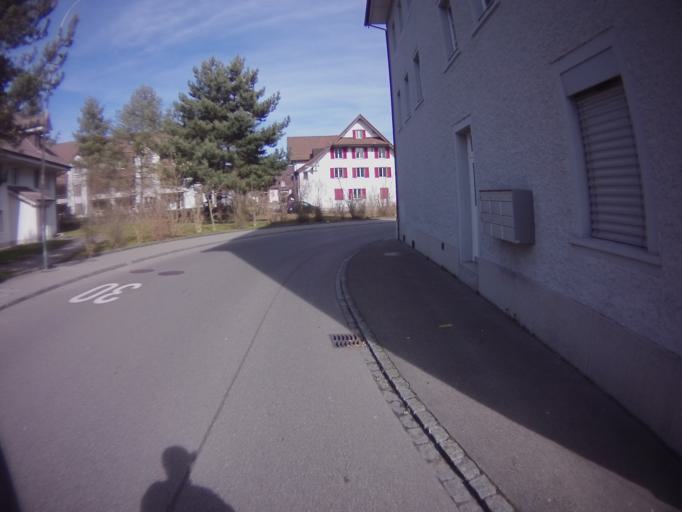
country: CH
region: Zurich
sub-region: Bezirk Dietikon
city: Dietikon
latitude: 47.4038
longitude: 8.3977
